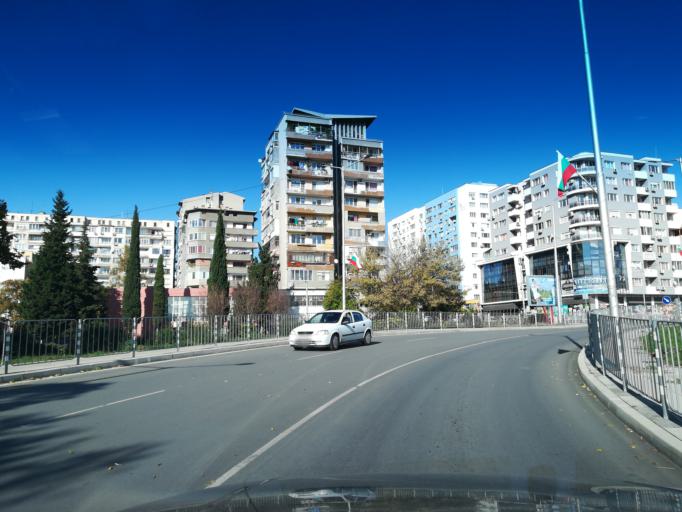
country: BG
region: Stara Zagora
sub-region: Obshtina Stara Zagora
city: Stara Zagora
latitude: 42.4213
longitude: 25.6352
